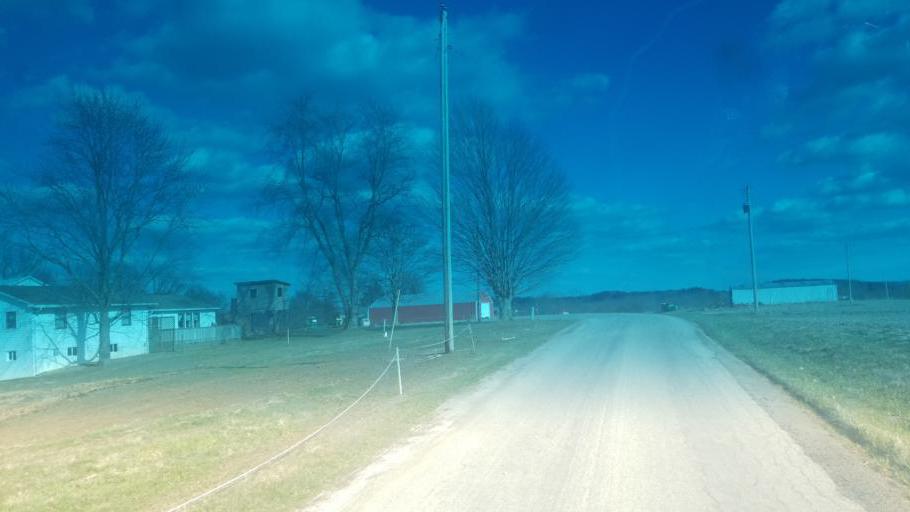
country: US
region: Ohio
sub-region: Highland County
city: Greenfield
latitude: 39.3005
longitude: -83.4394
